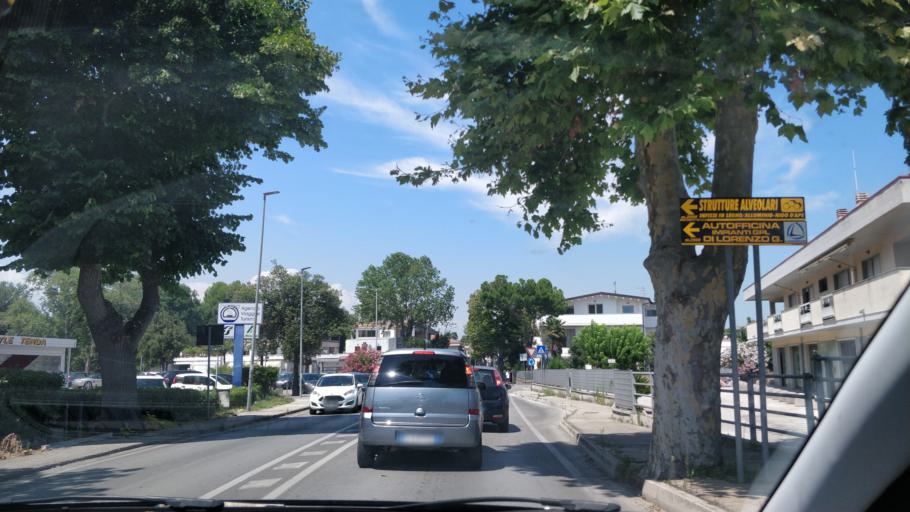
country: IT
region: Abruzzo
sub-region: Provincia di Chieti
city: Francavilla al Mare
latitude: 42.4246
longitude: 14.2781
